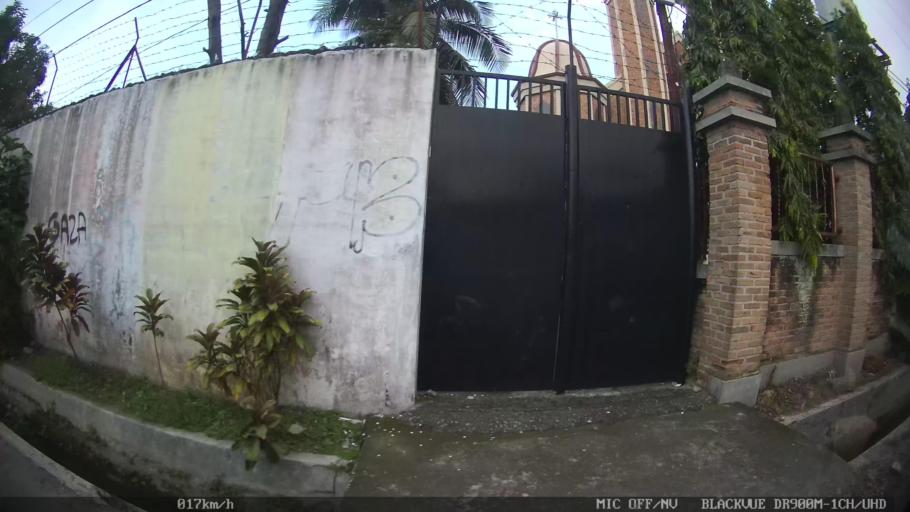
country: ID
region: North Sumatra
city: Medan
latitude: 3.6090
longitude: 98.6848
